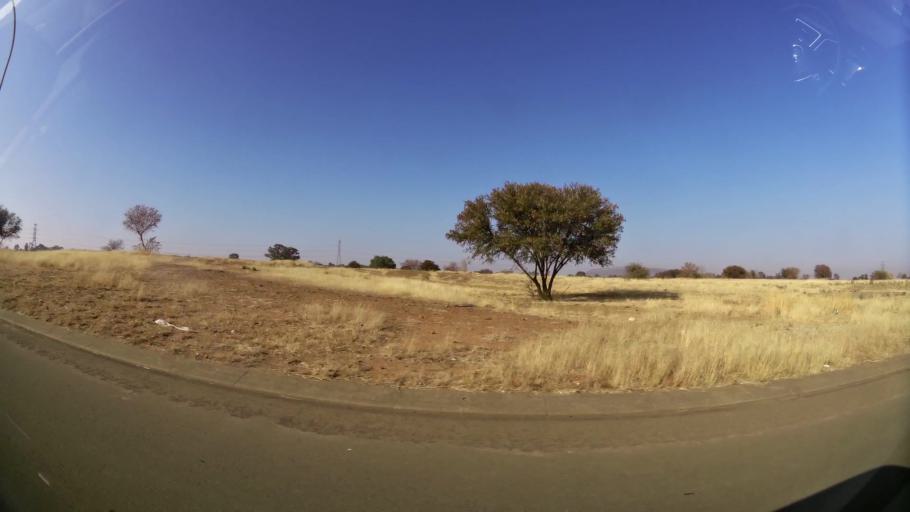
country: ZA
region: Orange Free State
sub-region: Mangaung Metropolitan Municipality
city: Bloemfontein
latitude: -29.1852
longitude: 26.1815
